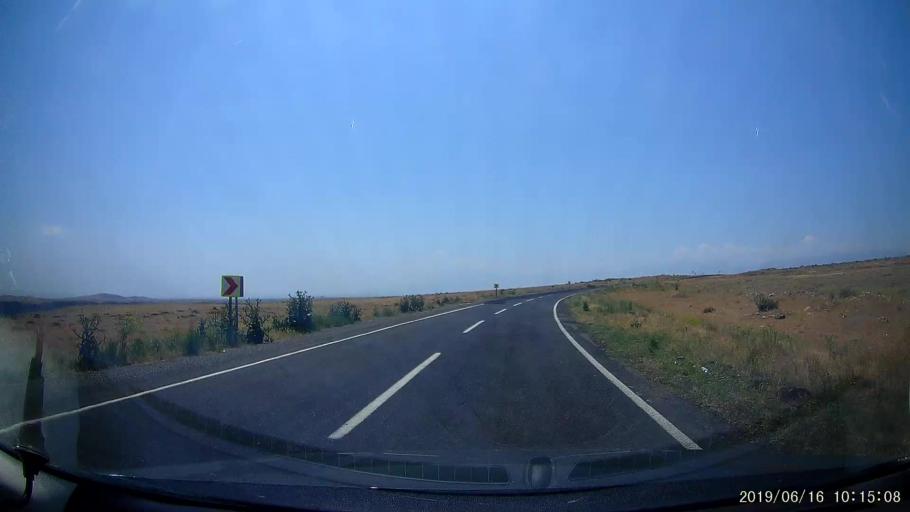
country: TR
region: Igdir
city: Tuzluca
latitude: 40.1788
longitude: 43.6765
